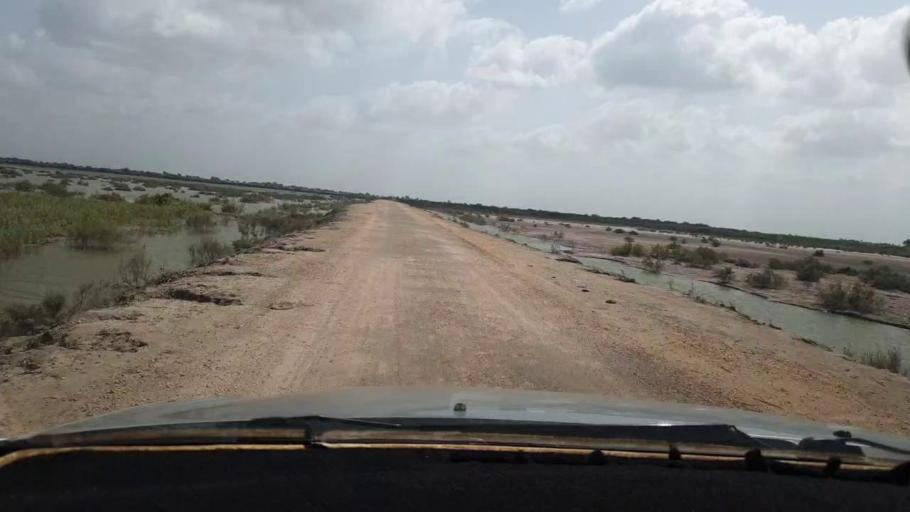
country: PK
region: Sindh
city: Tando Bago
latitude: 24.7207
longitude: 69.1514
